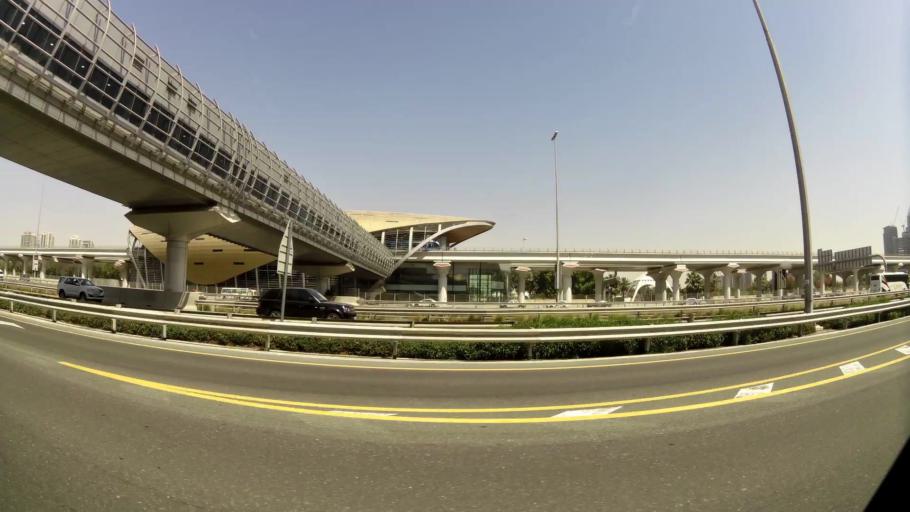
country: AE
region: Dubai
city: Dubai
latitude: 25.0893
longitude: 55.1569
